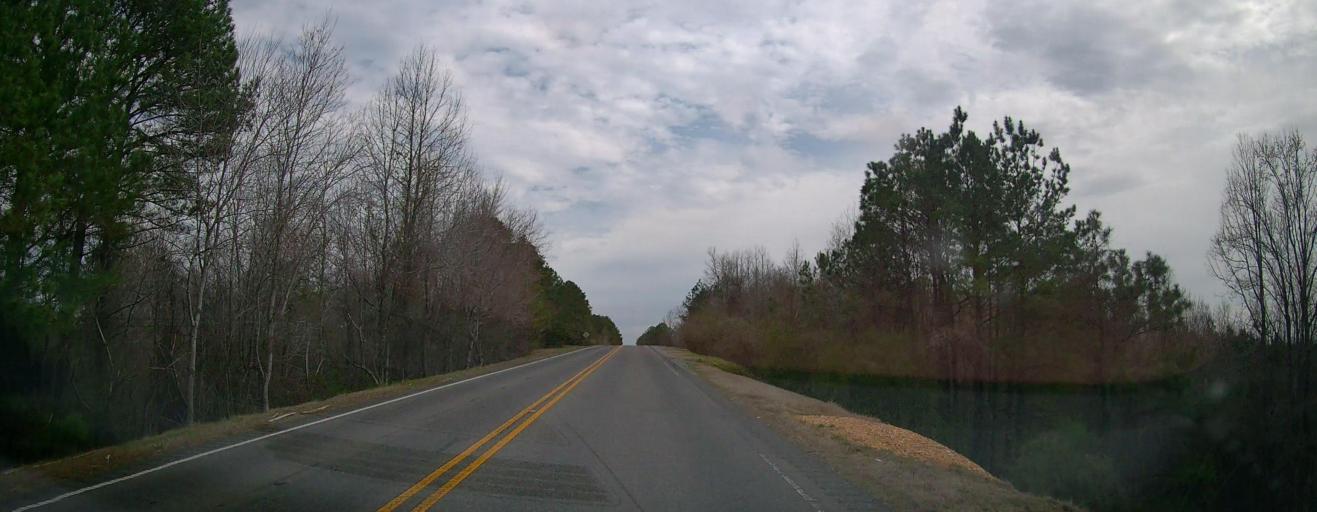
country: US
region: Alabama
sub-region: Marion County
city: Guin
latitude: 34.0484
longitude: -87.9633
